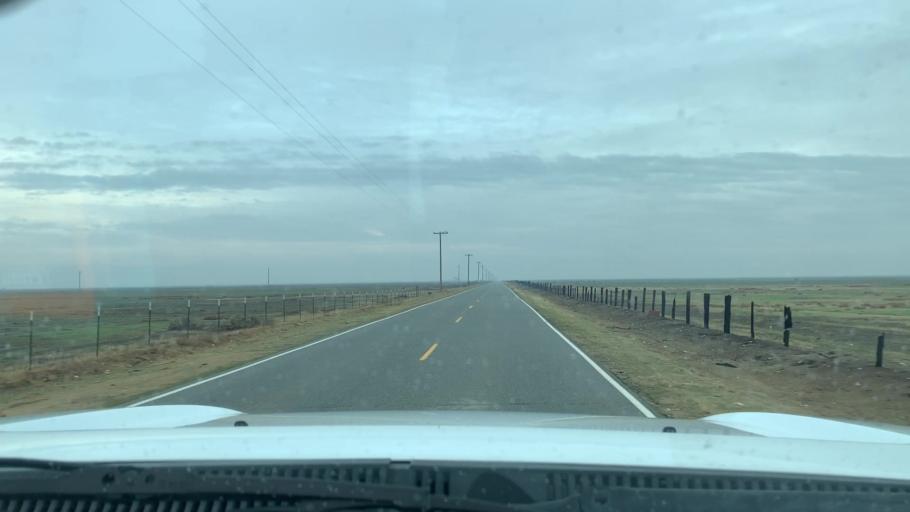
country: US
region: California
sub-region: Kern County
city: Lost Hills
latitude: 35.6786
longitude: -119.5798
